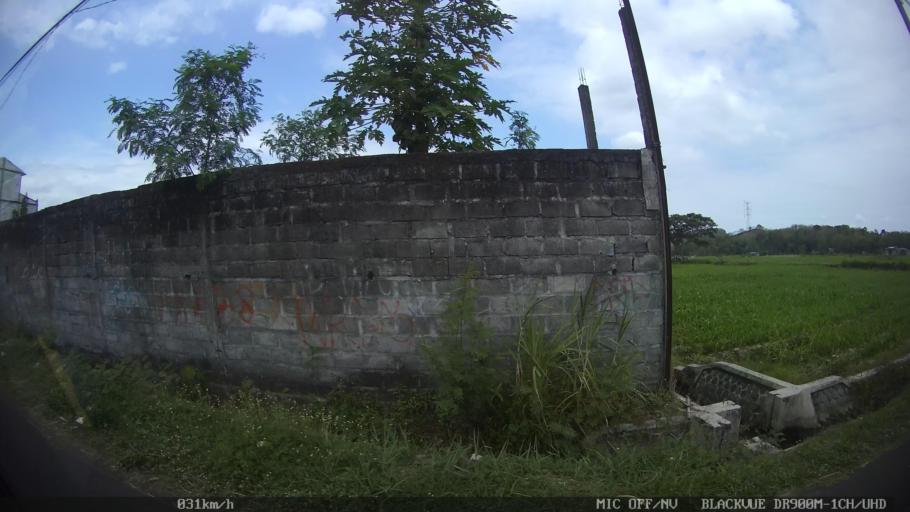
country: ID
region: Daerah Istimewa Yogyakarta
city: Depok
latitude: -7.8126
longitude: 110.4677
